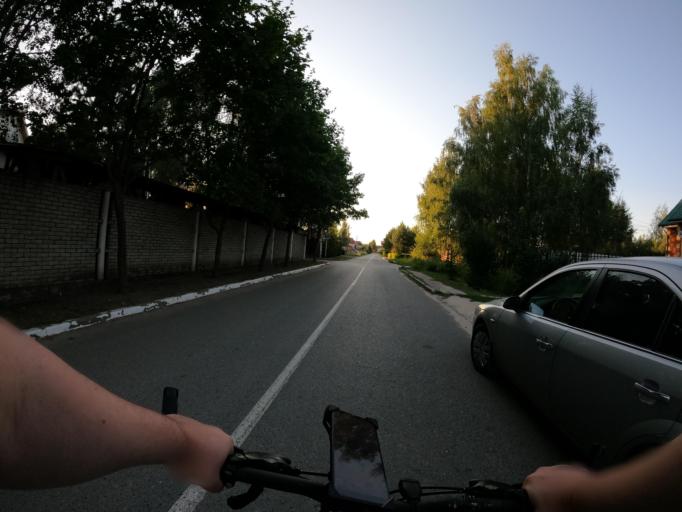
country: RU
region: Moskovskaya
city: Beloozerskiy
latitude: 55.4658
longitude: 38.4292
